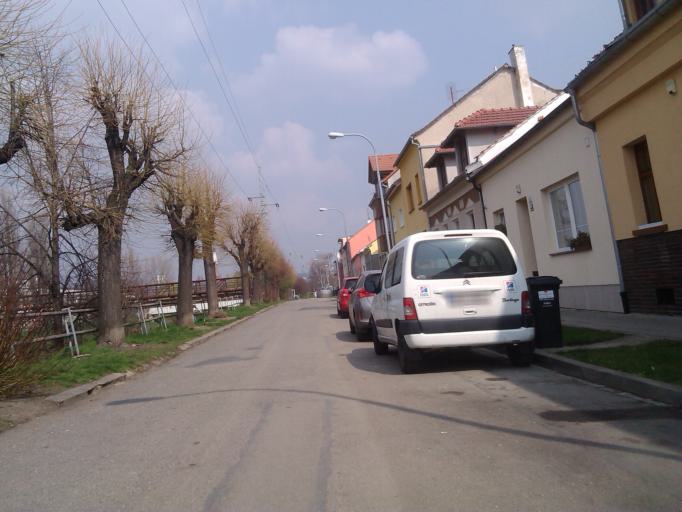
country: CZ
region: South Moravian
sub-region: Mesto Brno
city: Brno
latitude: 49.2093
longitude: 16.6372
